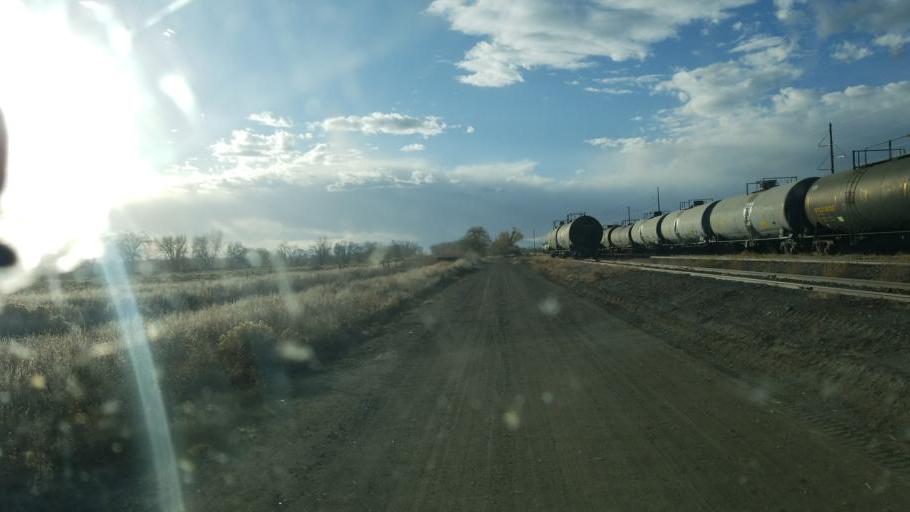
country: US
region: Colorado
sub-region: Alamosa County
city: Alamosa East
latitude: 37.4660
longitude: -105.8429
